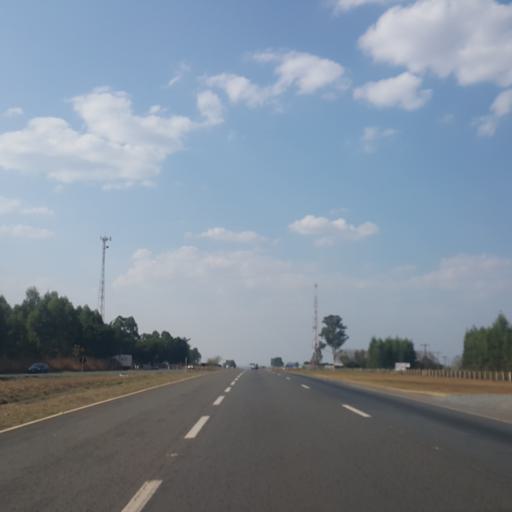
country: BR
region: Goias
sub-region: Abadiania
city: Abadiania
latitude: -16.2226
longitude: -48.7507
